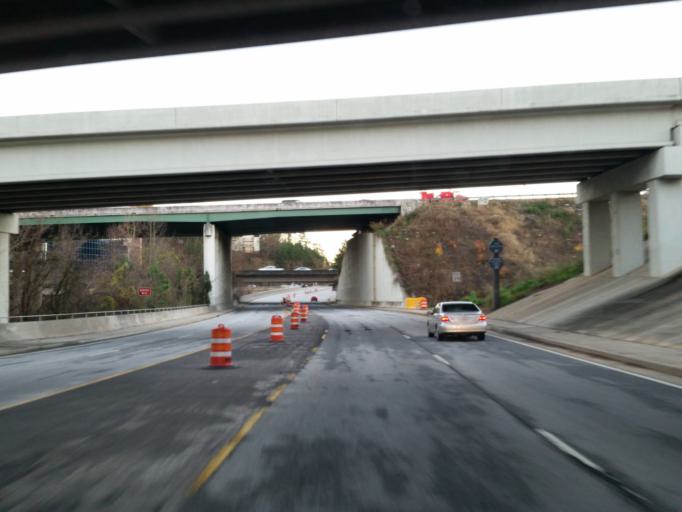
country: US
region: Georgia
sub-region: Cobb County
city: Vinings
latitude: 33.8930
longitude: -84.4578
